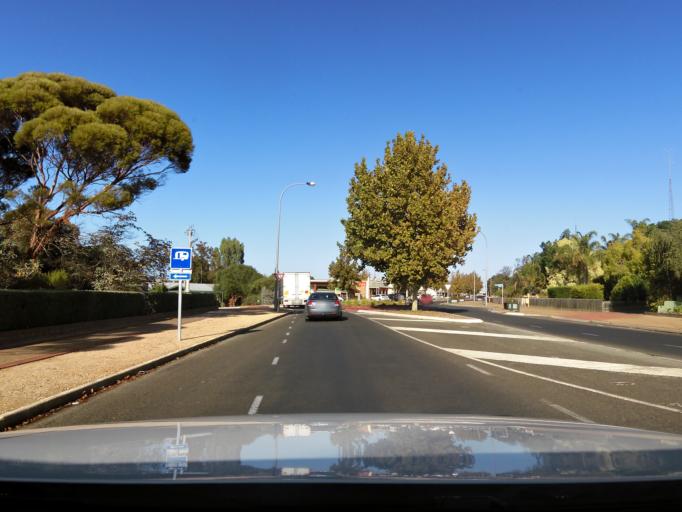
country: AU
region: South Australia
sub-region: Berri and Barmera
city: Berri
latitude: -34.2822
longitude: 140.6059
